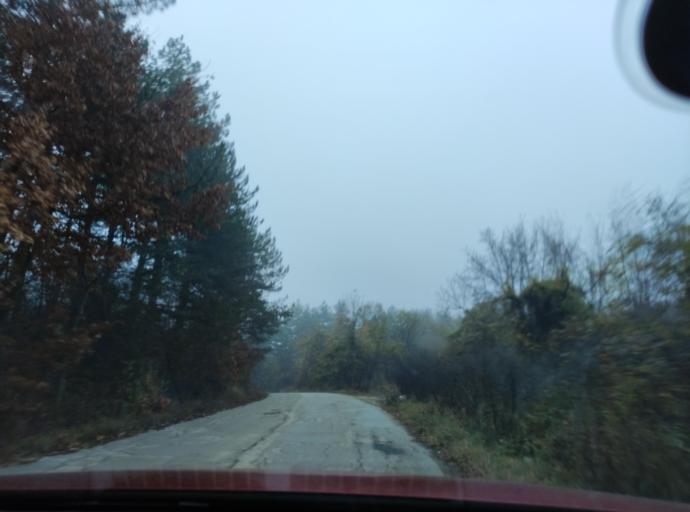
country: BG
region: Lovech
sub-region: Obshtina Yablanitsa
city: Yablanitsa
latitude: 43.1050
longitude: 24.0666
